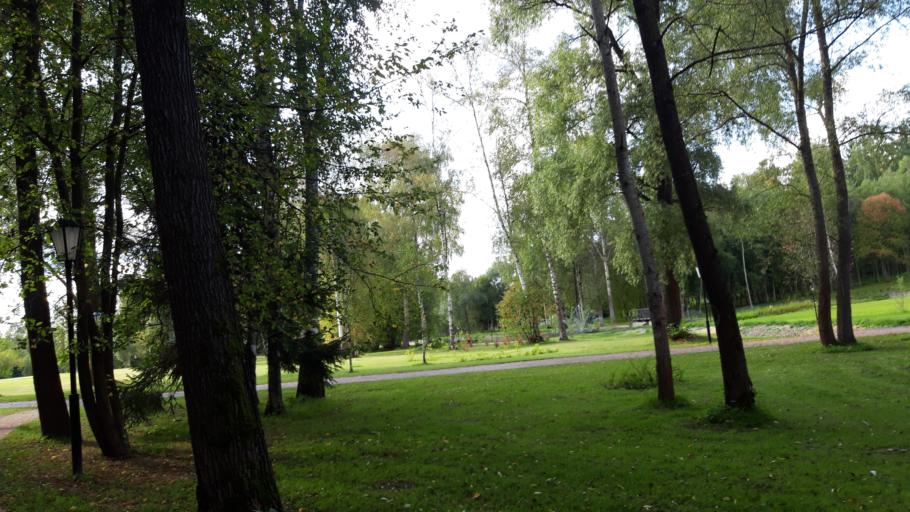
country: RU
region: Moskovskaya
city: Mendeleyevo
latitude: 56.0480
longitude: 37.2218
